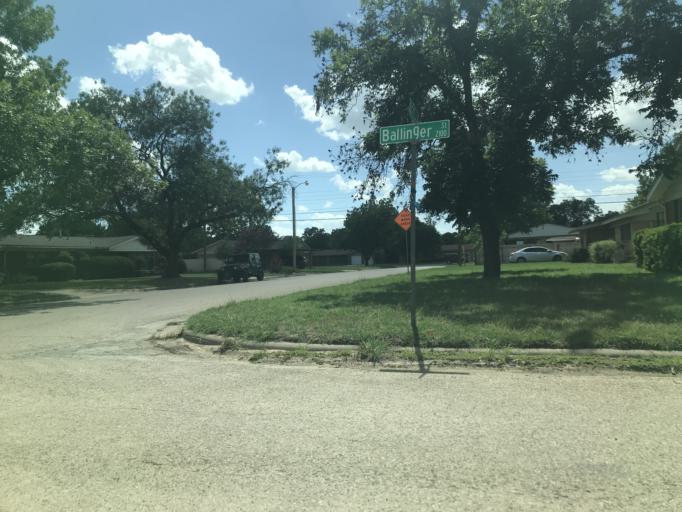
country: US
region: Texas
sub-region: Taylor County
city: Abilene
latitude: 32.4227
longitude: -99.7624
